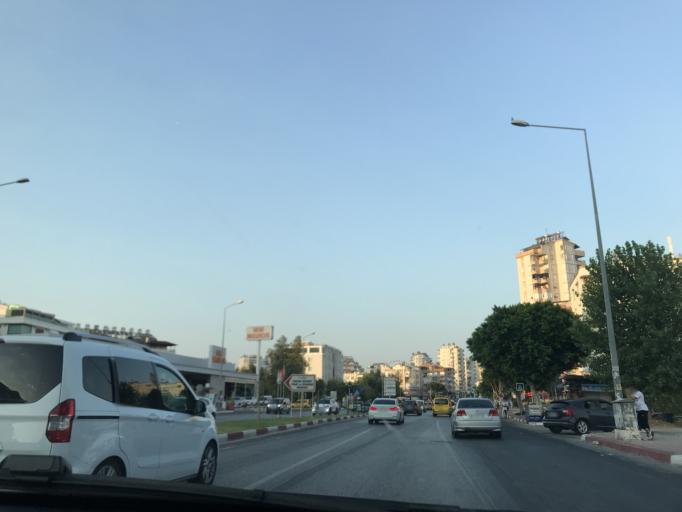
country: TR
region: Antalya
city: Antalya
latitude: 36.8783
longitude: 30.6478
